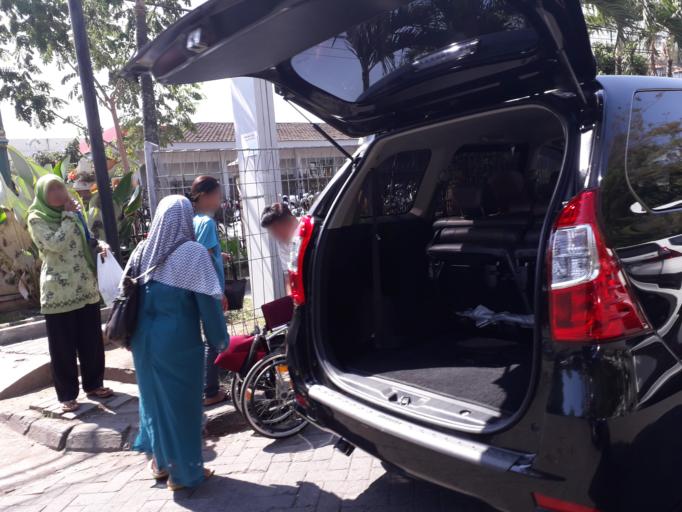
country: ID
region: Daerah Istimewa Yogyakarta
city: Yogyakarta
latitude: -7.7693
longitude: 110.3737
